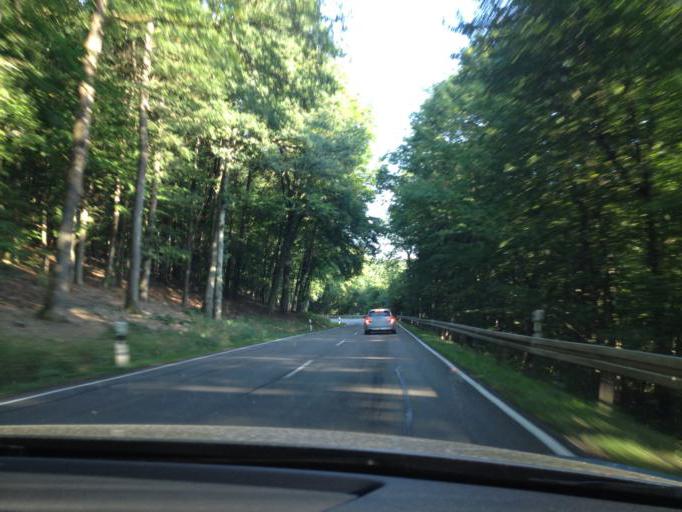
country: DE
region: Saarland
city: Tholey
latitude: 49.5192
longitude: 7.0501
